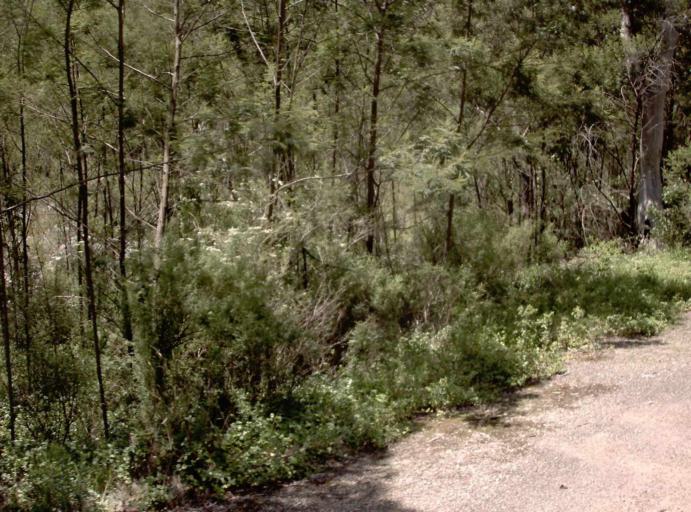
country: AU
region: Victoria
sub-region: East Gippsland
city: Bairnsdale
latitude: -37.4842
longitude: 147.8317
